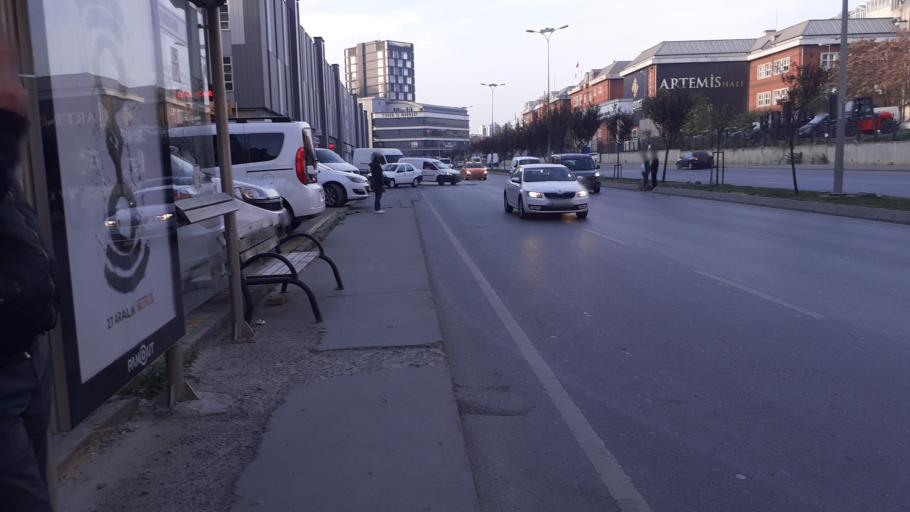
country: TR
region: Istanbul
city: Basaksehir
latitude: 41.0710
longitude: 28.7951
